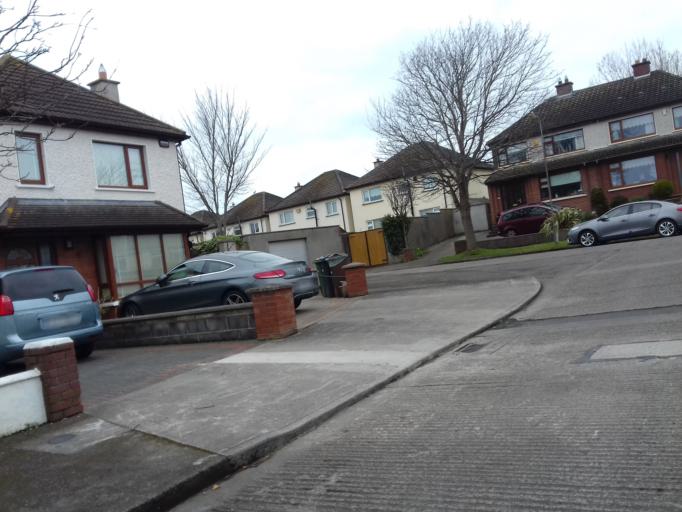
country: IE
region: Leinster
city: Portmarnock
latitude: 53.4308
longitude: -6.1290
